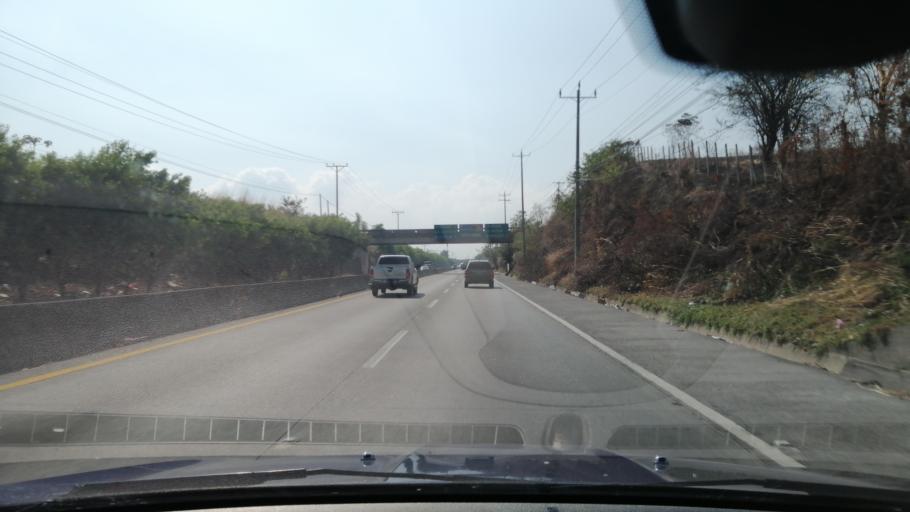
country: SV
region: San Salvador
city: Ayutuxtepeque
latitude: 13.7877
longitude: -89.2186
